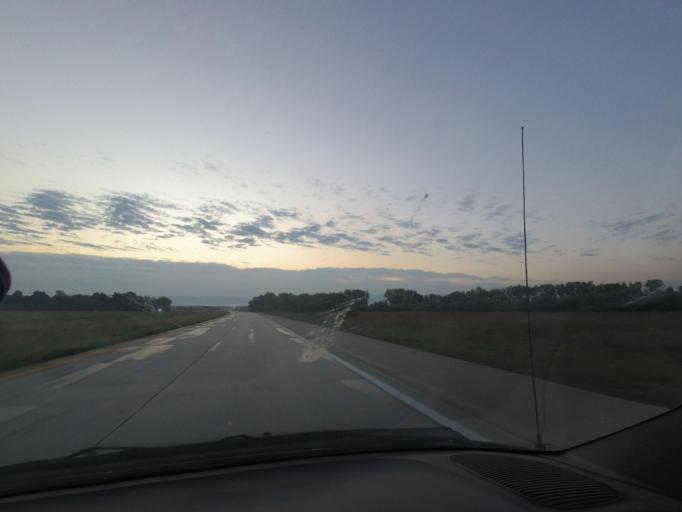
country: US
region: Missouri
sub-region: Linn County
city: Marceline
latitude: 39.7609
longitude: -92.7175
